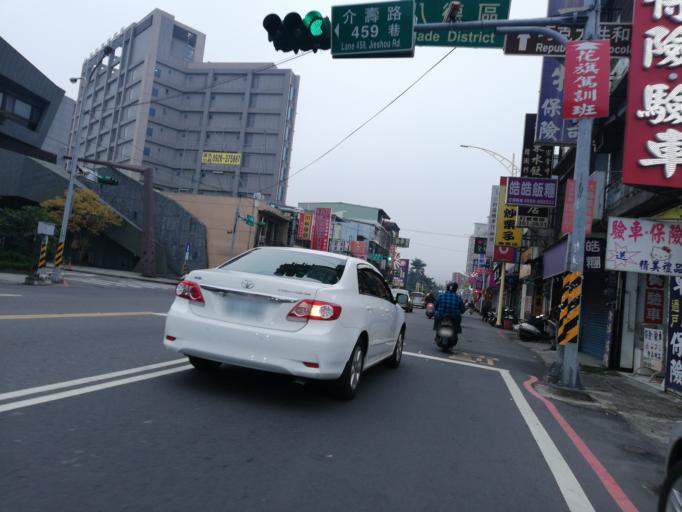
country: TW
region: Taiwan
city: Taoyuan City
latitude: 24.9784
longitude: 121.3038
